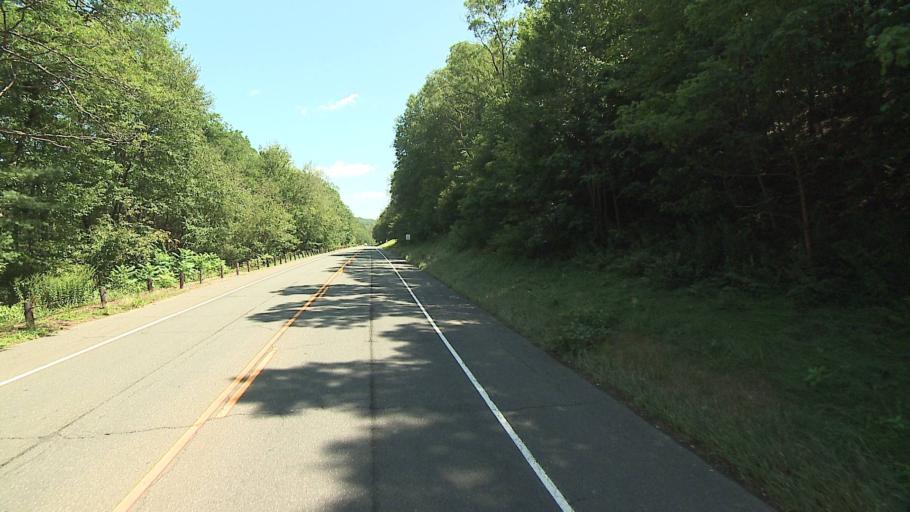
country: US
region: Connecticut
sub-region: Hartford County
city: Collinsville
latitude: 41.7765
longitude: -72.9146
